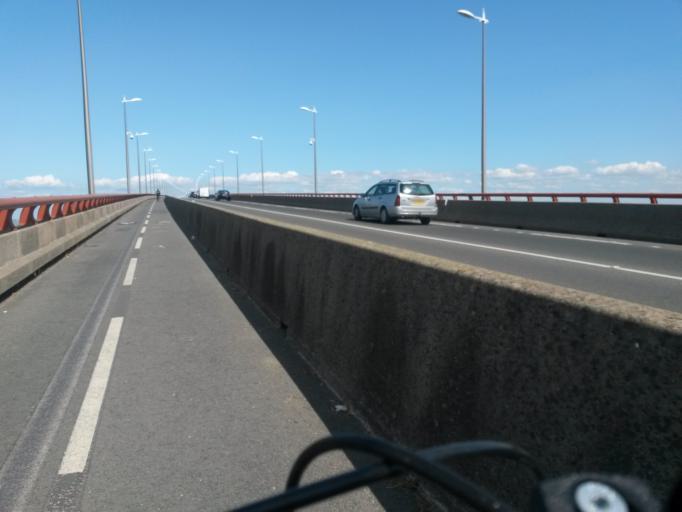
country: FR
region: Poitou-Charentes
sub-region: Departement de la Charente-Maritime
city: Rivedoux-Plage
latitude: 46.1663
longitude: -1.2522
